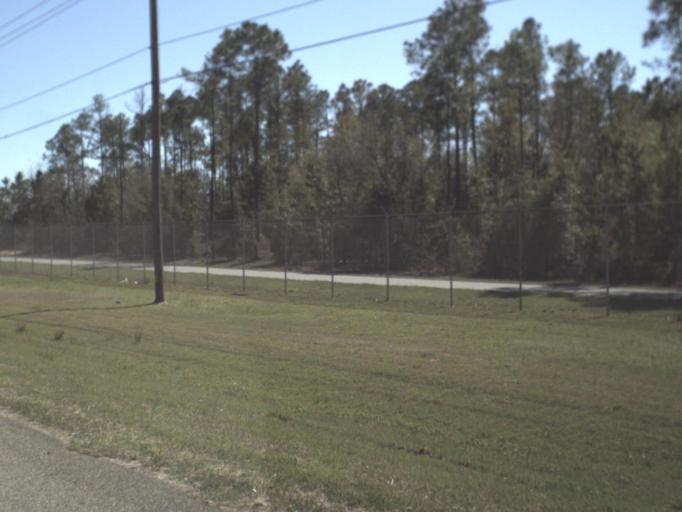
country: US
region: Florida
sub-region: Leon County
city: Tallahassee
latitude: 30.3956
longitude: -84.3243
